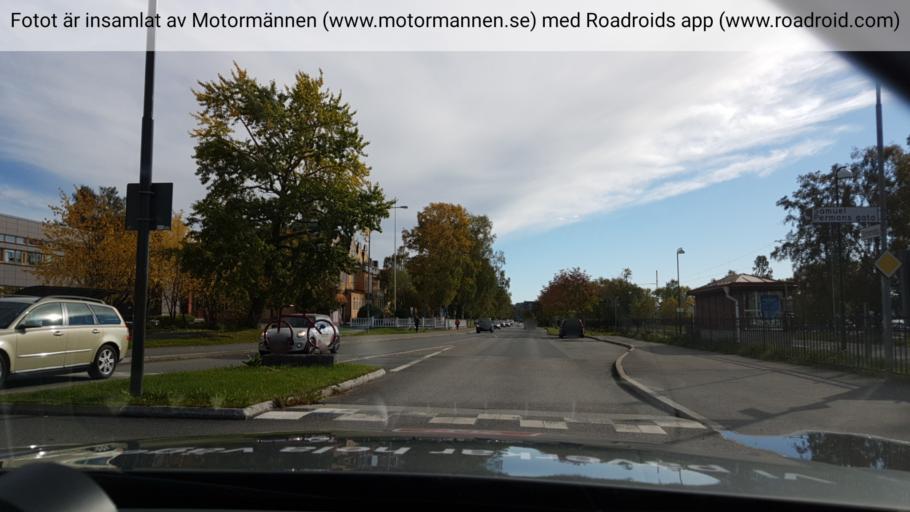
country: SE
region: Jaemtland
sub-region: OEstersunds Kommun
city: Ostersund
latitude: 63.1791
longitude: 14.6315
